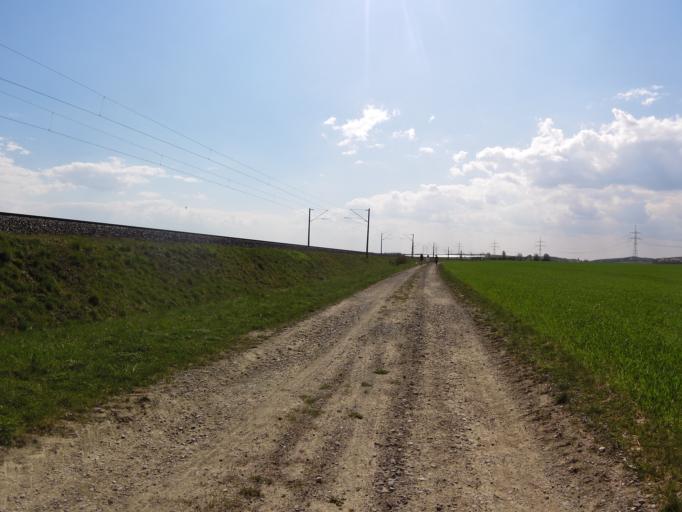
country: DE
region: Bavaria
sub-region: Regierungsbezirk Unterfranken
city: Oberpleichfeld
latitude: 49.8406
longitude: 10.0999
